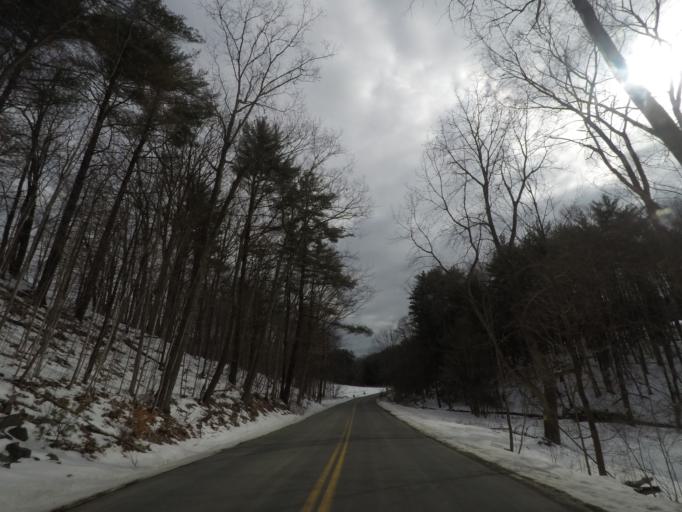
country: US
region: New York
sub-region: Rensselaer County
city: Hoosick Falls
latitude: 42.8836
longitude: -73.4178
